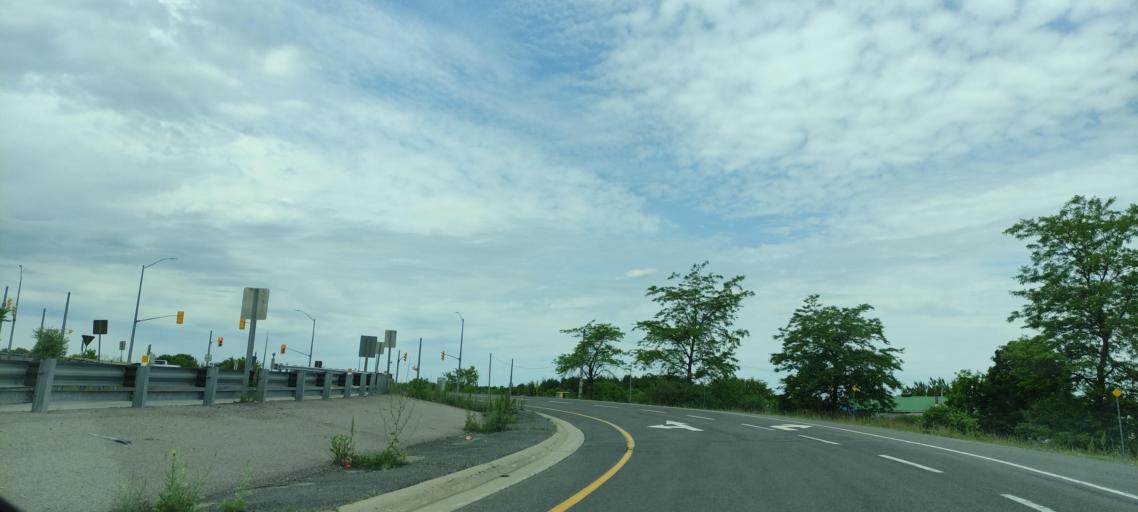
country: CA
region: Ontario
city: Cobourg
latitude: 43.9814
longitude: -78.1953
